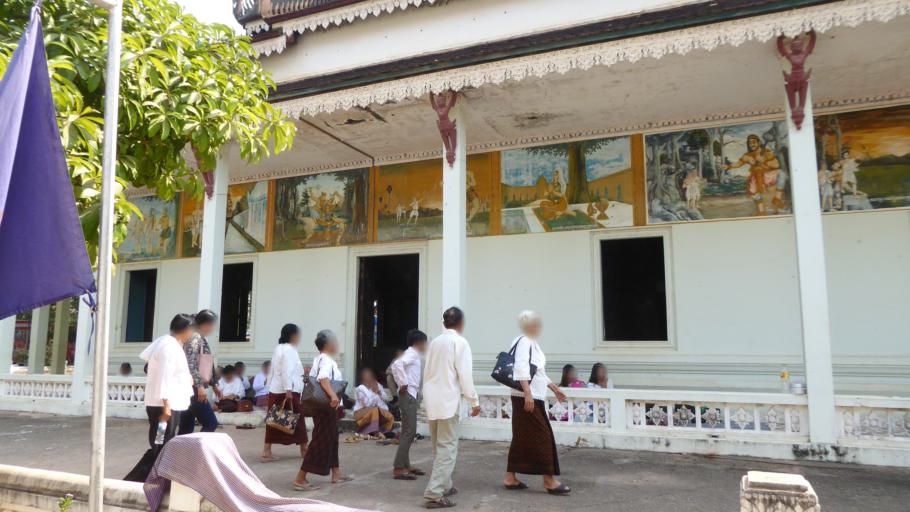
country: KH
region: Siem Reap
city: Siem Reap
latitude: 13.4132
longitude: 103.8639
